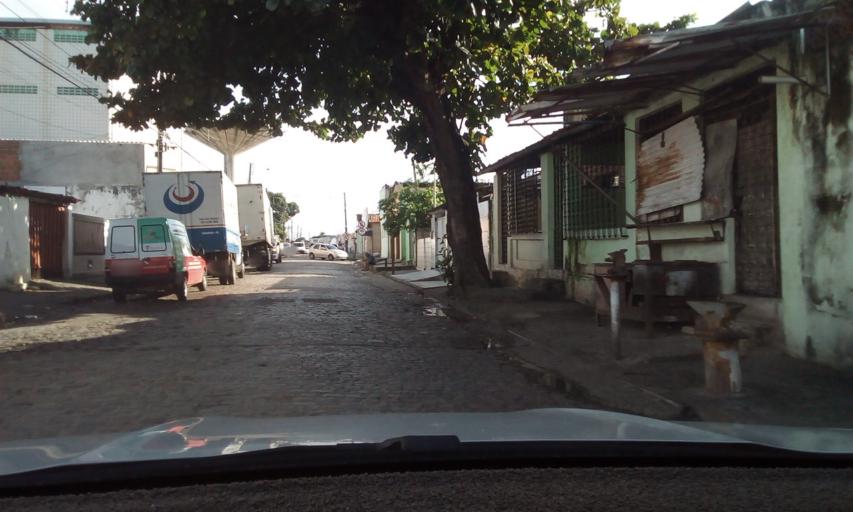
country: BR
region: Paraiba
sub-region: Joao Pessoa
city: Joao Pessoa
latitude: -7.1378
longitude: -34.8885
